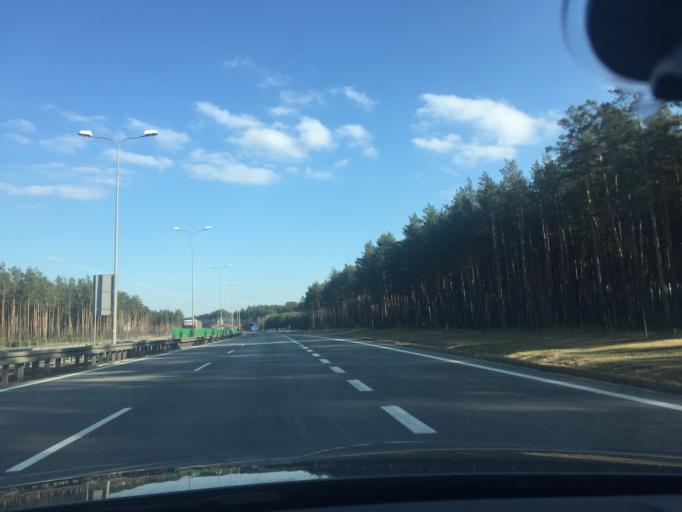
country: PL
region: Lubusz
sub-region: Powiat slubicki
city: Rzepin
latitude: 52.3342
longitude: 14.9102
